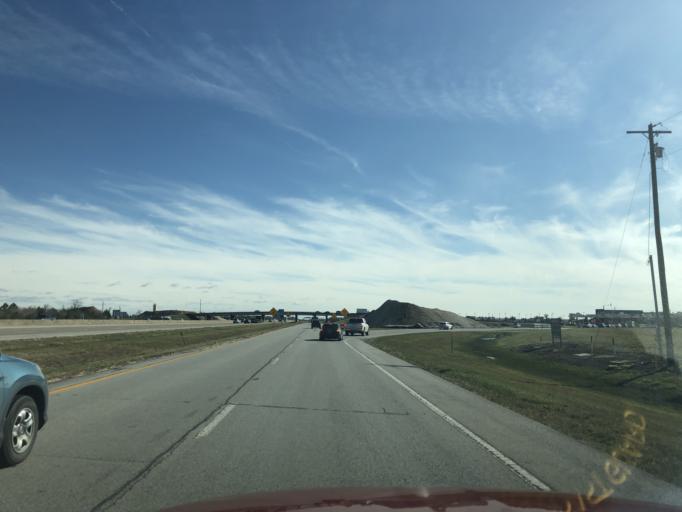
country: US
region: Texas
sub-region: Galveston County
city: Dickinson
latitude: 29.4332
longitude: -95.0635
